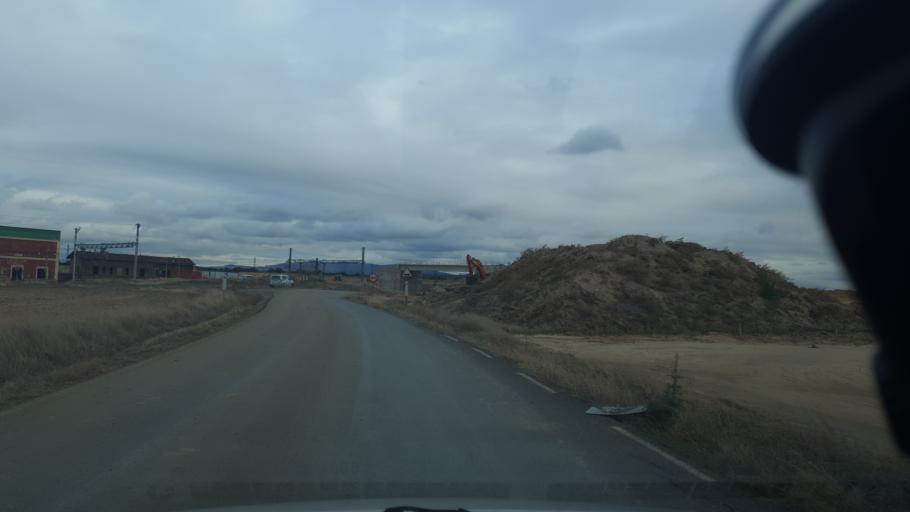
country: ES
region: Castille and Leon
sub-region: Provincia de Avila
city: Velayos
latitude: 40.8299
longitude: -4.6052
